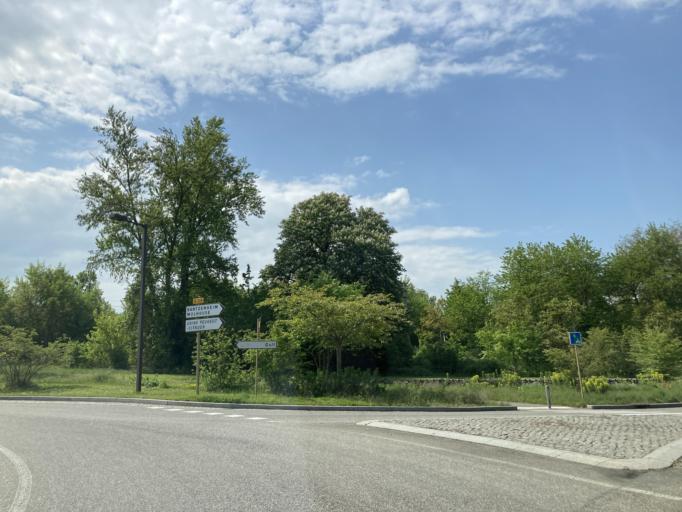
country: FR
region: Alsace
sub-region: Departement du Haut-Rhin
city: Chalampe
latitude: 47.8161
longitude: 7.5392
